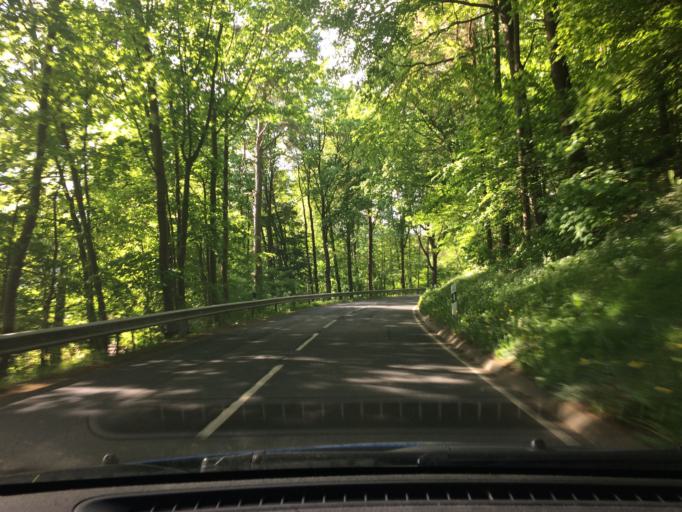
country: DE
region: Lower Saxony
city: Buhren
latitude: 51.5128
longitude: 9.5925
